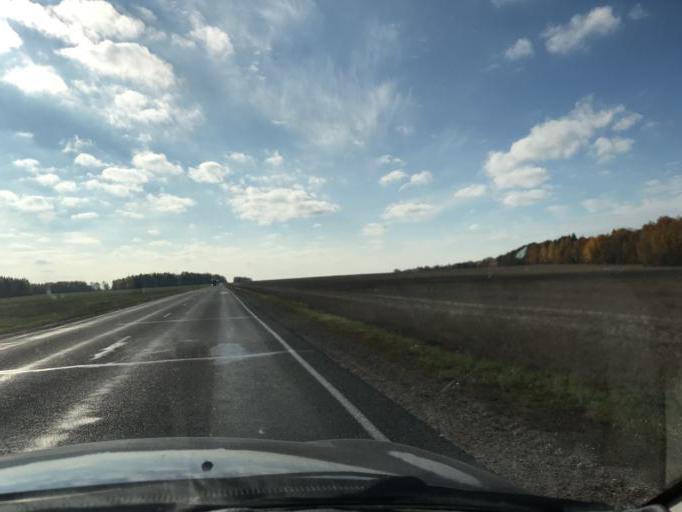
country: BY
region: Grodnenskaya
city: Voranava
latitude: 54.1985
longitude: 25.3469
